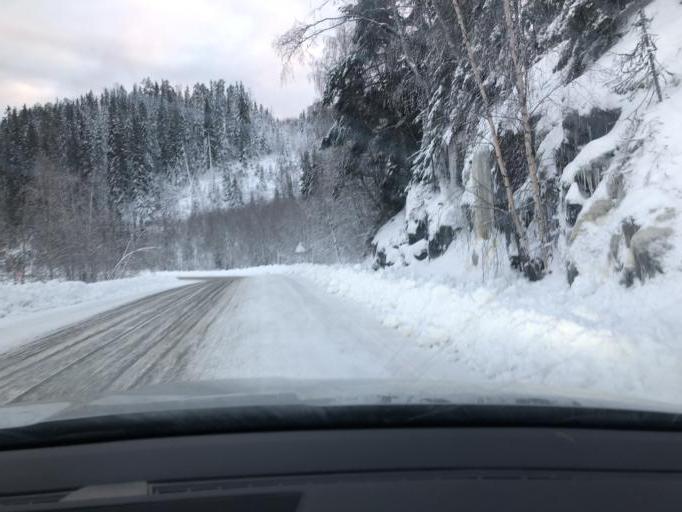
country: SE
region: Vaesternorrland
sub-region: Kramfors Kommun
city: Nordingra
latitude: 62.9515
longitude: 18.2461
